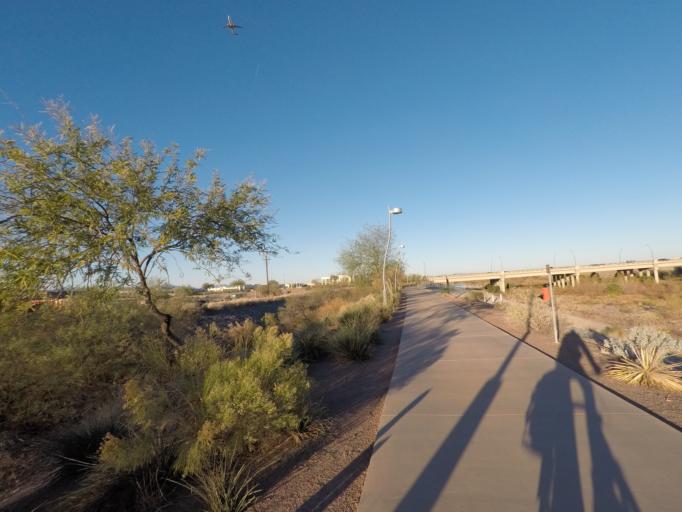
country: US
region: Arizona
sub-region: Maricopa County
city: Tempe Junction
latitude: 33.4336
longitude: -111.9590
